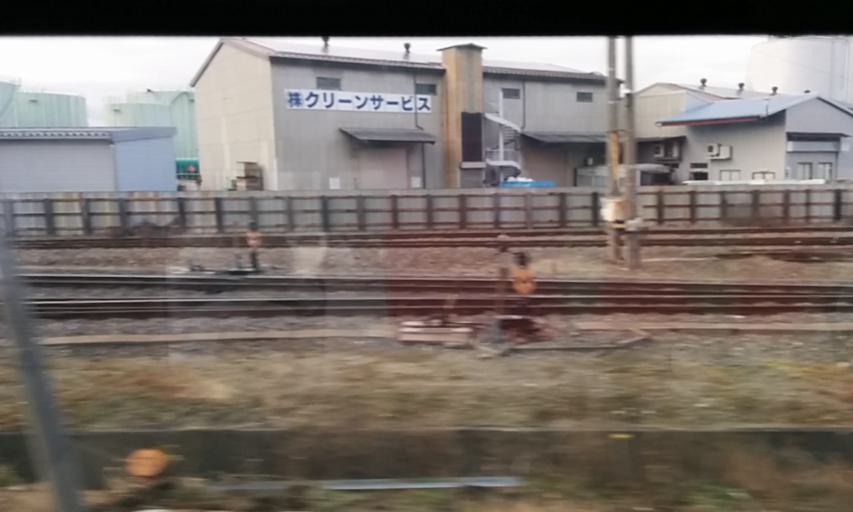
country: JP
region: Nagano
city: Matsumoto
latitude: 36.2002
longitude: 137.9658
